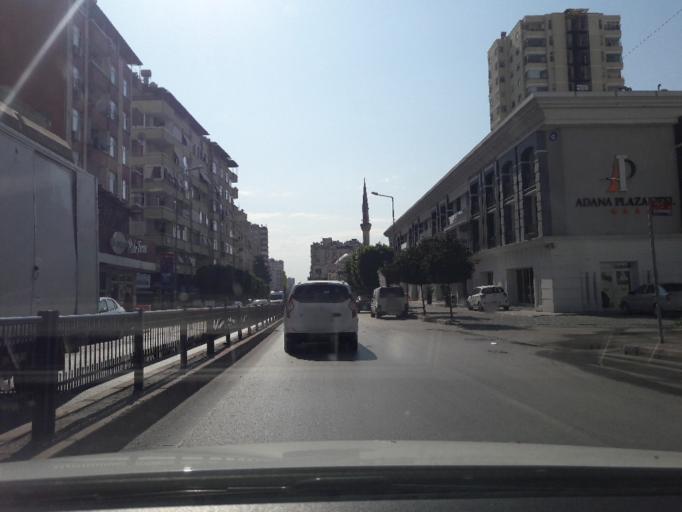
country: TR
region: Adana
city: Adana
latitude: 37.0132
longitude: 35.3226
